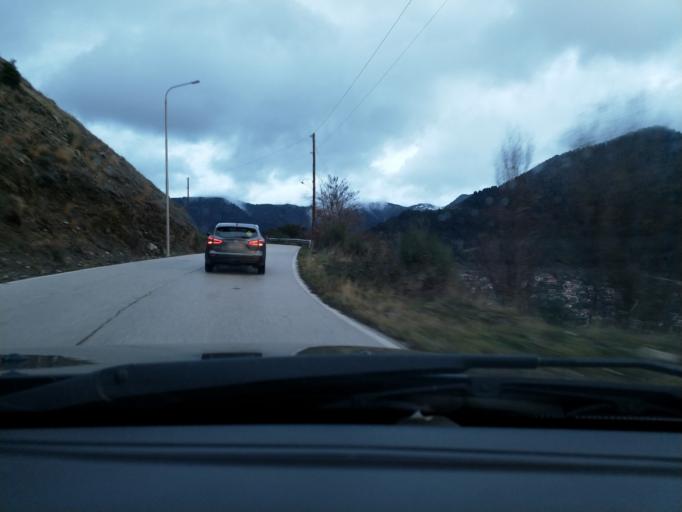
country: GR
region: Epirus
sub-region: Nomos Ioanninon
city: Metsovo
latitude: 39.7645
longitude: 21.1758
